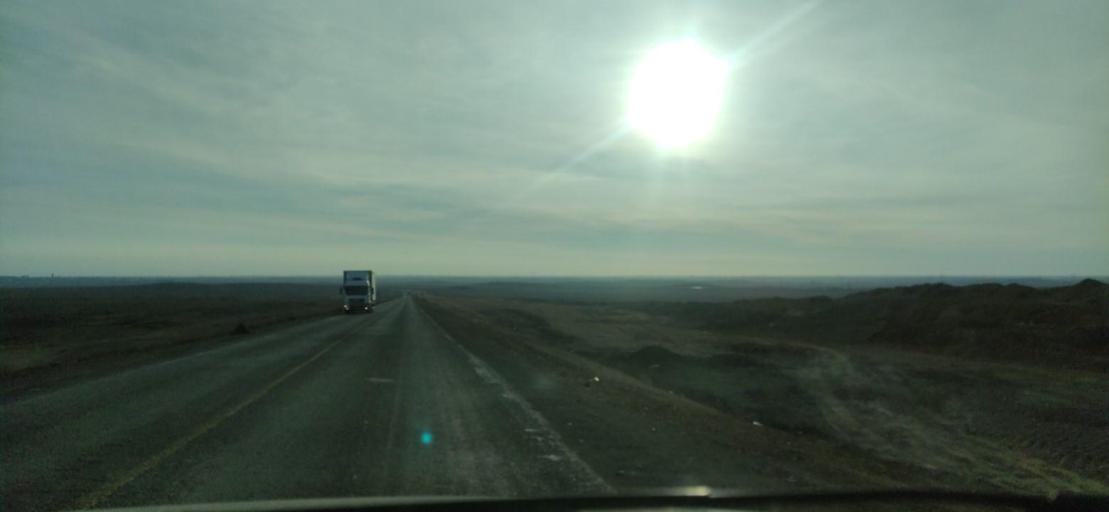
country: KZ
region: Qaraghandy
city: Saryshaghan
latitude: 46.1639
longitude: 73.6149
